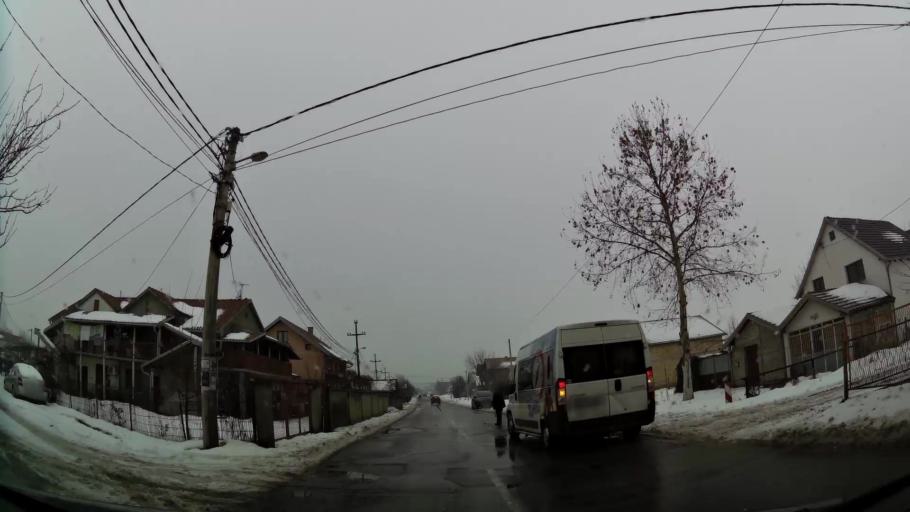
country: RS
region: Central Serbia
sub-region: Belgrade
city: Zemun
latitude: 44.8585
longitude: 20.3286
